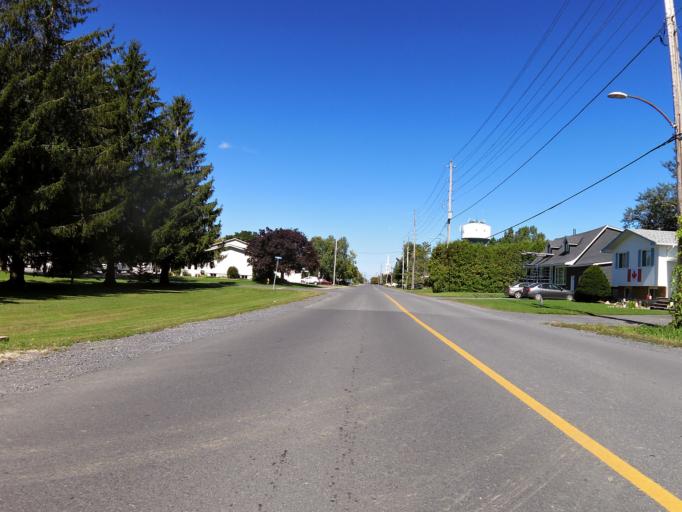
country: CA
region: Ontario
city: Casselman
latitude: 45.2683
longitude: -75.2721
